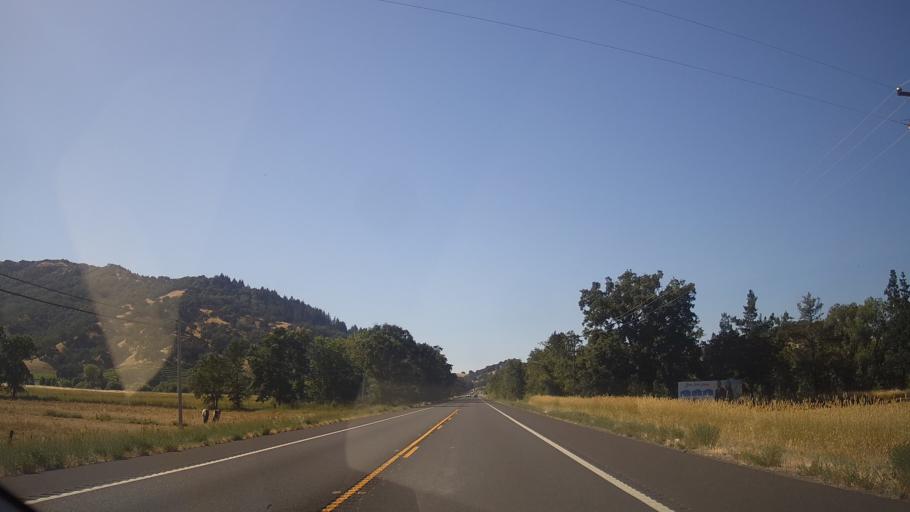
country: US
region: California
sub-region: Mendocino County
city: Talmage
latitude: 39.0465
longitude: -123.1519
